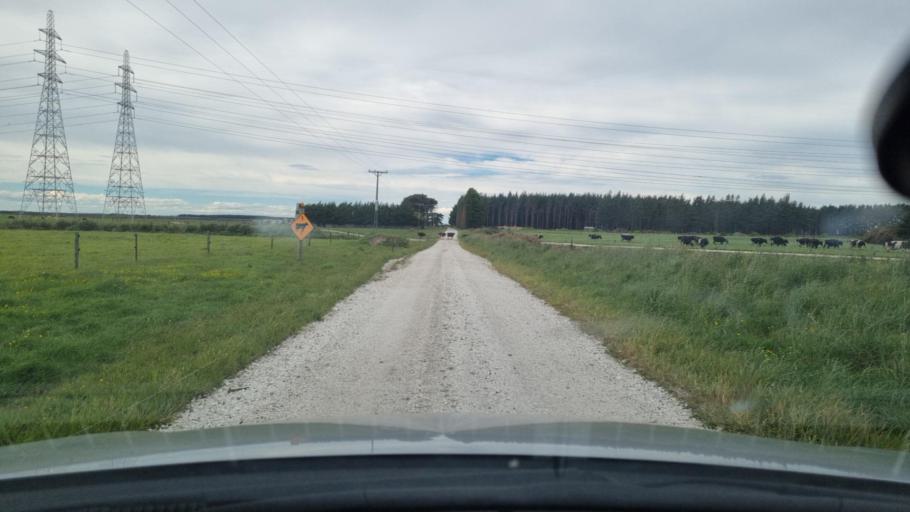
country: NZ
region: Southland
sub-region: Invercargill City
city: Invercargill
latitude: -46.4917
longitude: 168.4340
